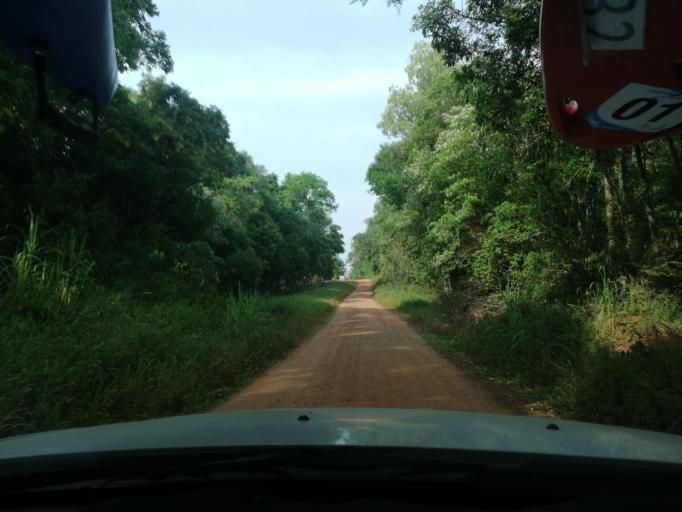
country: AR
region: Misiones
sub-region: Departamento de San Ignacio
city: San Ignacio
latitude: -27.2987
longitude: -55.5737
